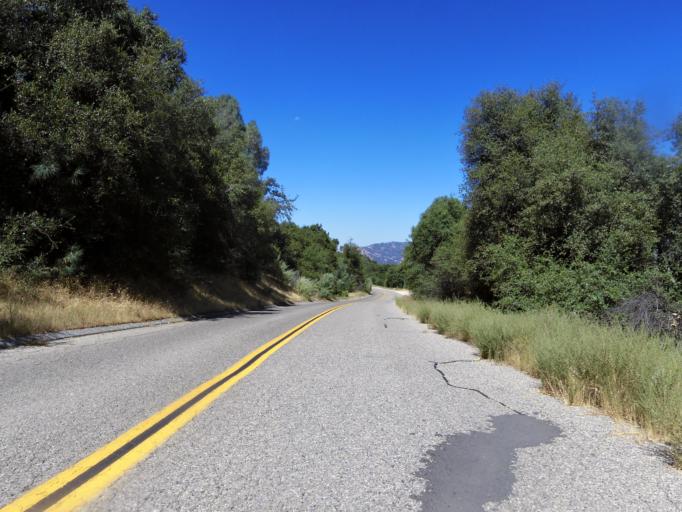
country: US
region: California
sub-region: Madera County
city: Ahwahnee
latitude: 37.3601
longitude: -119.6870
